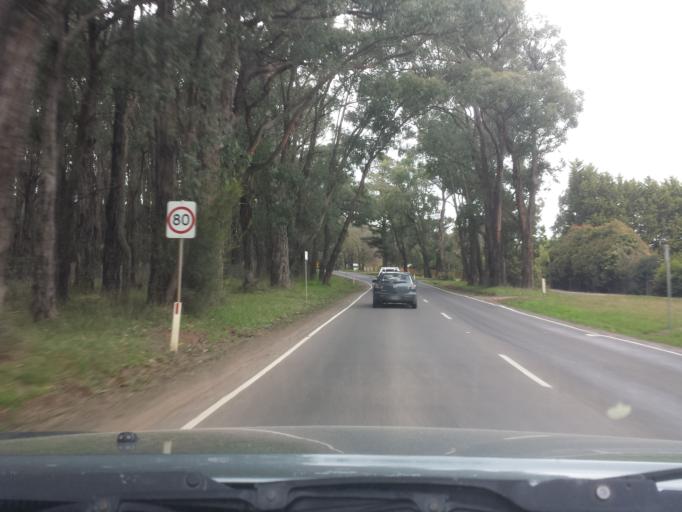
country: AU
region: Victoria
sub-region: Yarra Ranges
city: Monbulk
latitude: -37.8313
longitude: 145.4274
